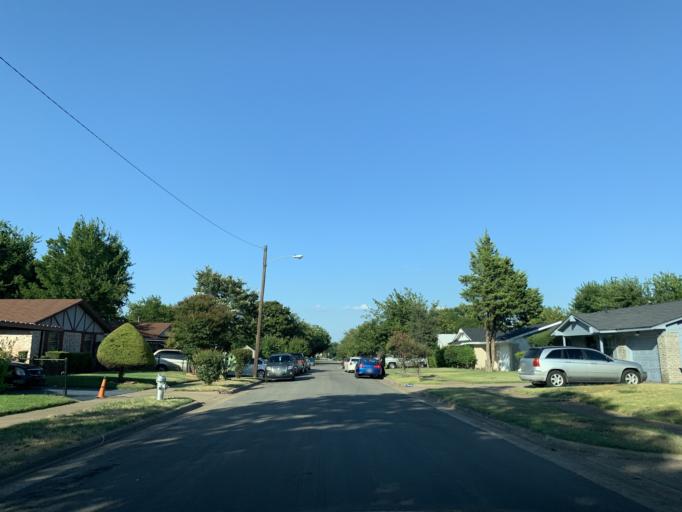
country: US
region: Texas
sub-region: Dallas County
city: Hutchins
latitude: 32.6645
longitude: -96.7647
